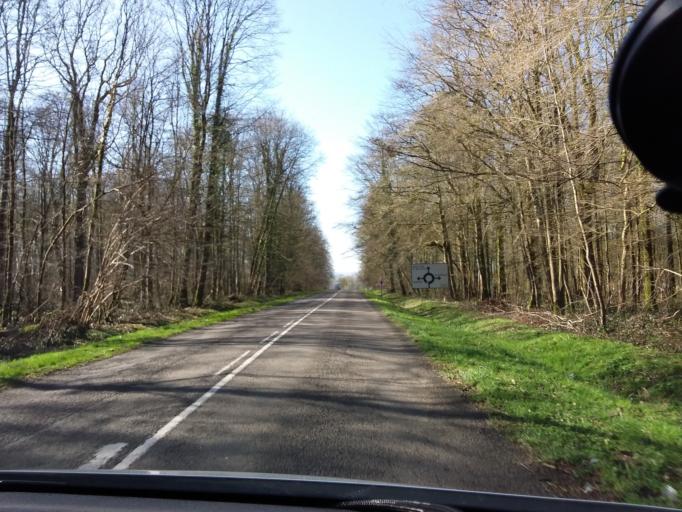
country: FR
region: Picardie
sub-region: Departement de l'Aisne
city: Hirson
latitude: 49.9405
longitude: 4.0732
